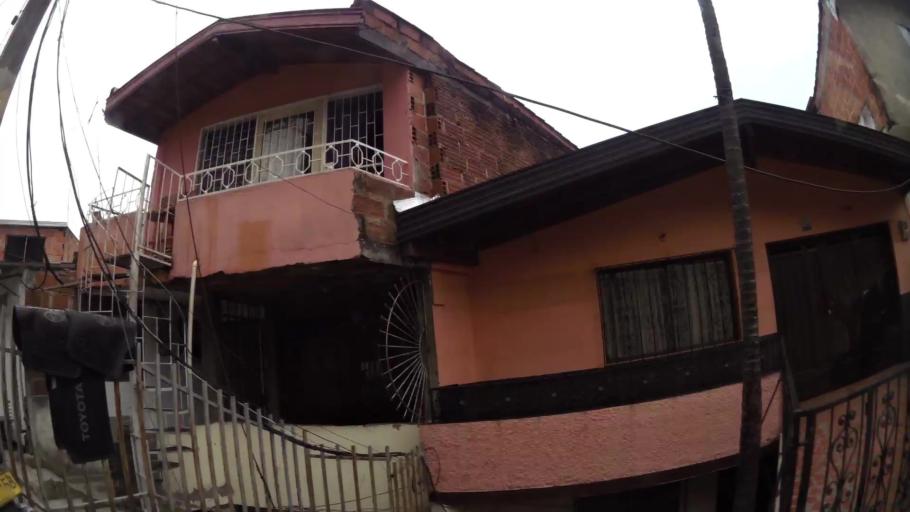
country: CO
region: Antioquia
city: Medellin
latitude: 6.2839
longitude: -75.5471
